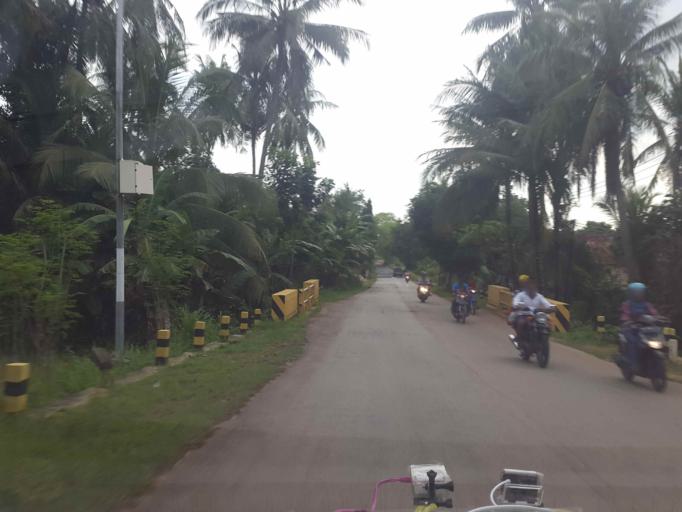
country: ID
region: East Java
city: Giring Barat
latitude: -6.9703
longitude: 113.8633
